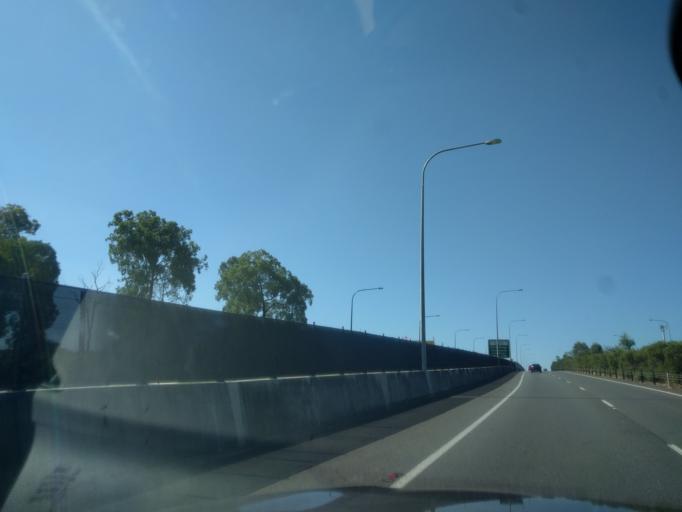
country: AU
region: Queensland
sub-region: Logan
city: Park Ridge South
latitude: -27.7088
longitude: 153.0379
